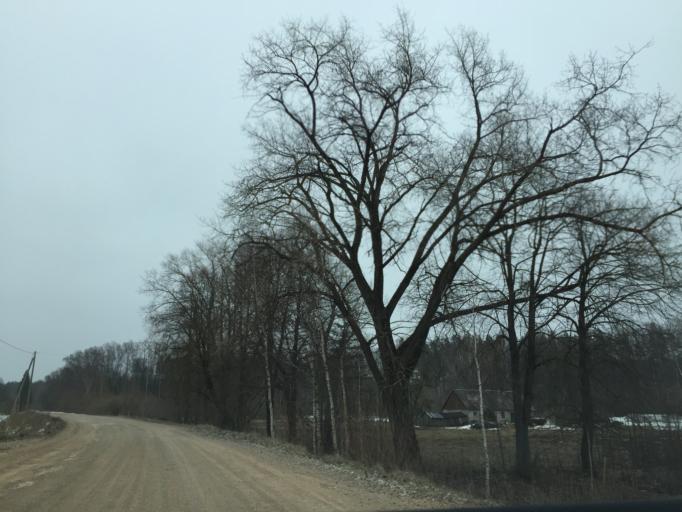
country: LV
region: Ozolnieku
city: Ozolnieki
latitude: 56.6325
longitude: 23.8049
